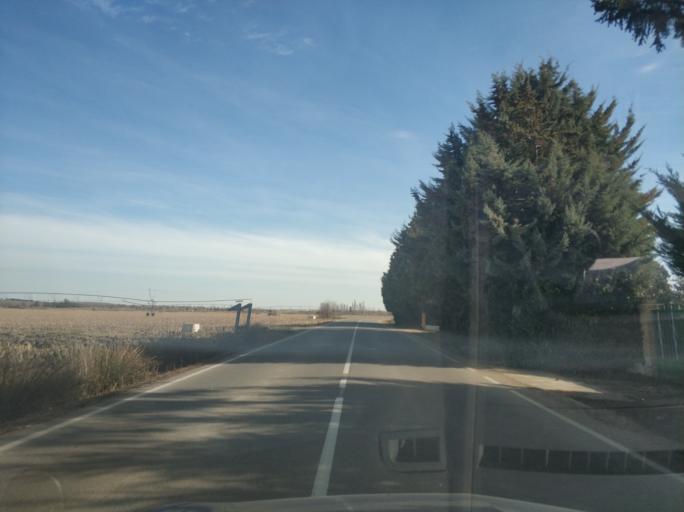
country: ES
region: Castille and Leon
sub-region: Provincia de Salamanca
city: Valverdon
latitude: 41.0351
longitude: -5.7695
